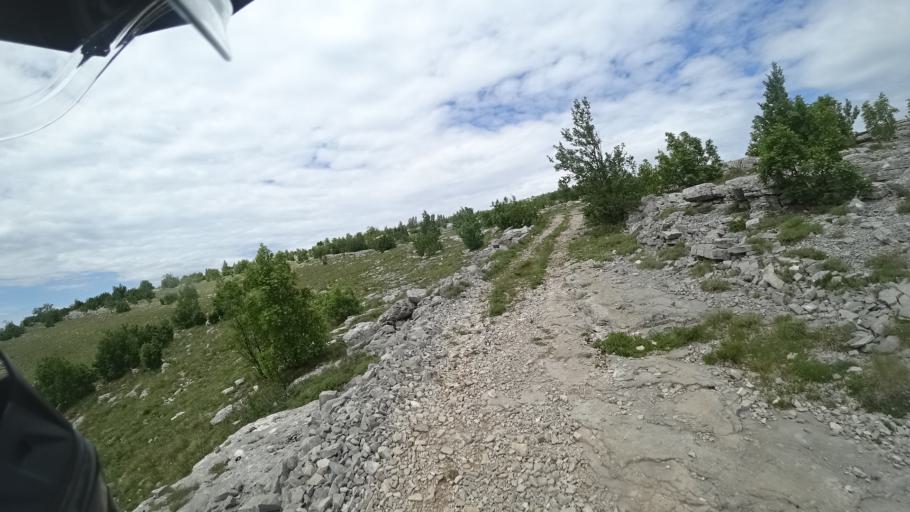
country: HR
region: Splitsko-Dalmatinska
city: Hrvace
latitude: 43.8906
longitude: 16.5851
